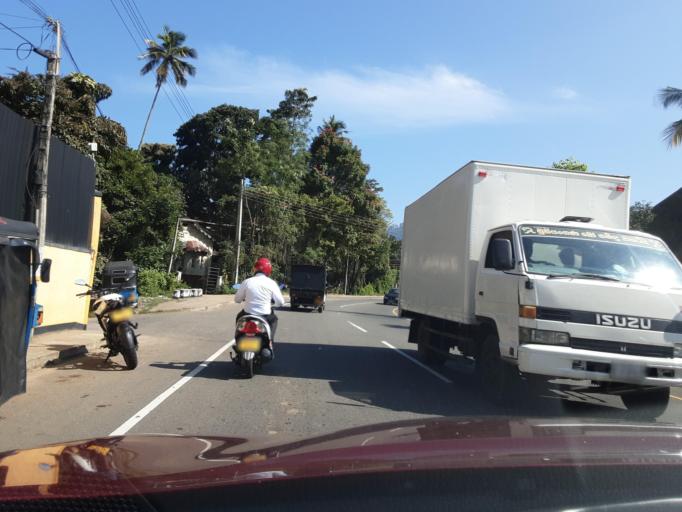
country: LK
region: Uva
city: Badulla
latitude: 6.9930
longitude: 81.0567
